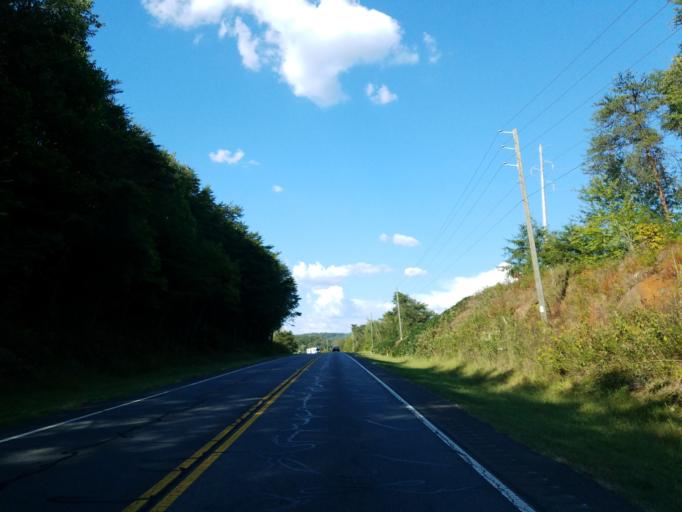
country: US
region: Georgia
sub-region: Bartow County
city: Rydal
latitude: 34.3731
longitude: -84.7107
